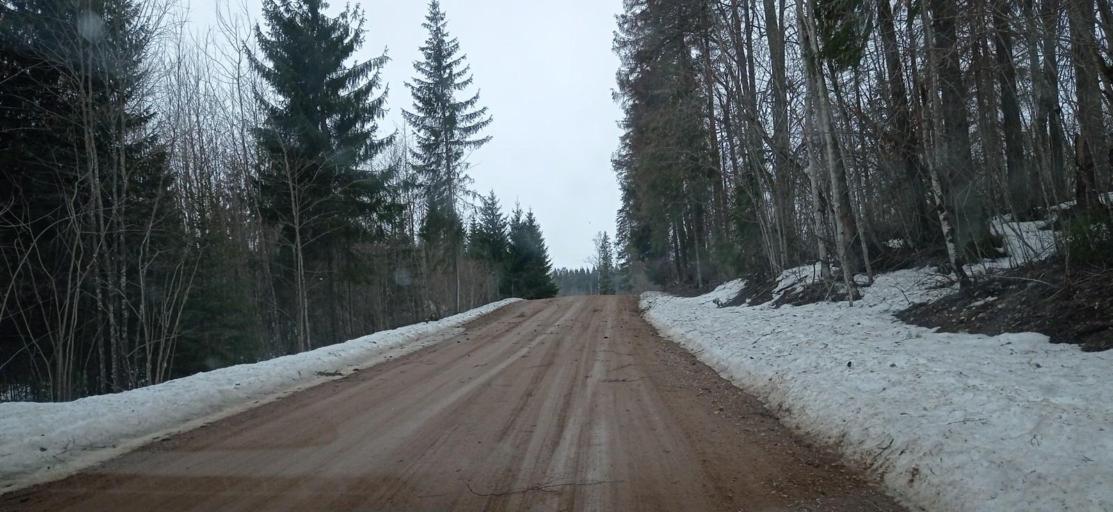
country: EE
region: Tartu
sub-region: UElenurme vald
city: Ulenurme
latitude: 58.1223
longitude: 26.7002
